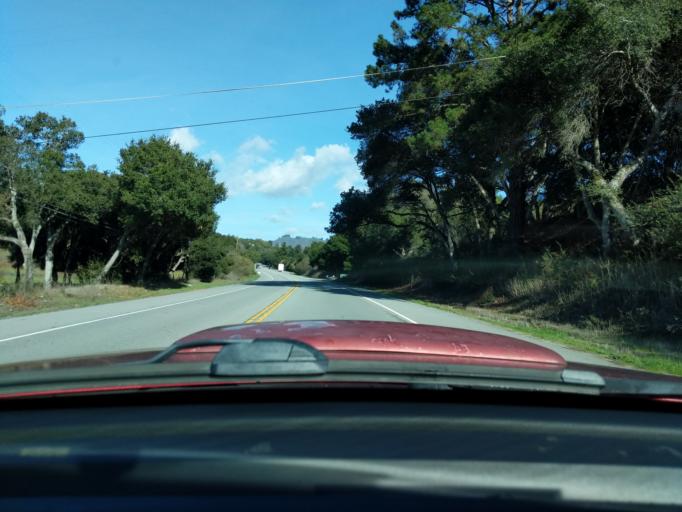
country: US
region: California
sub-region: San Benito County
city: Aromas
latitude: 36.8771
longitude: -121.6630
